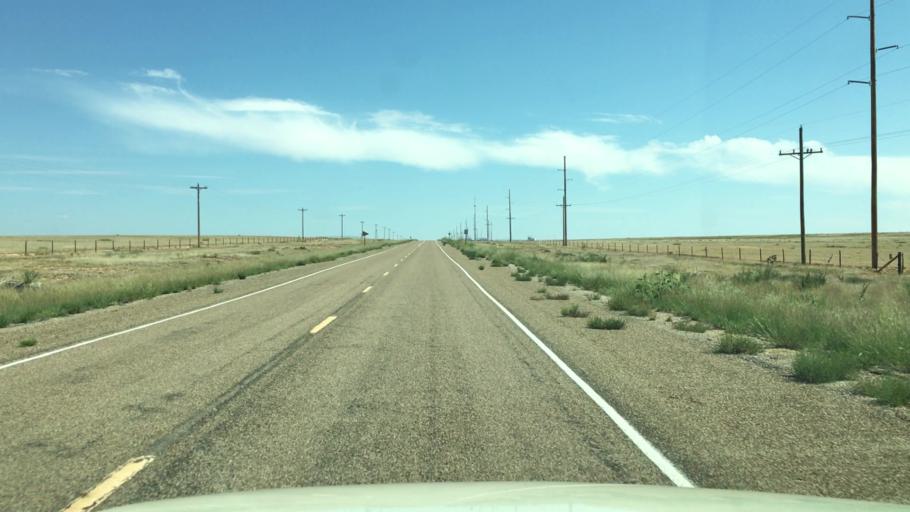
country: US
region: New Mexico
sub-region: Chaves County
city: Roswell
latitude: 33.9496
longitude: -104.5886
